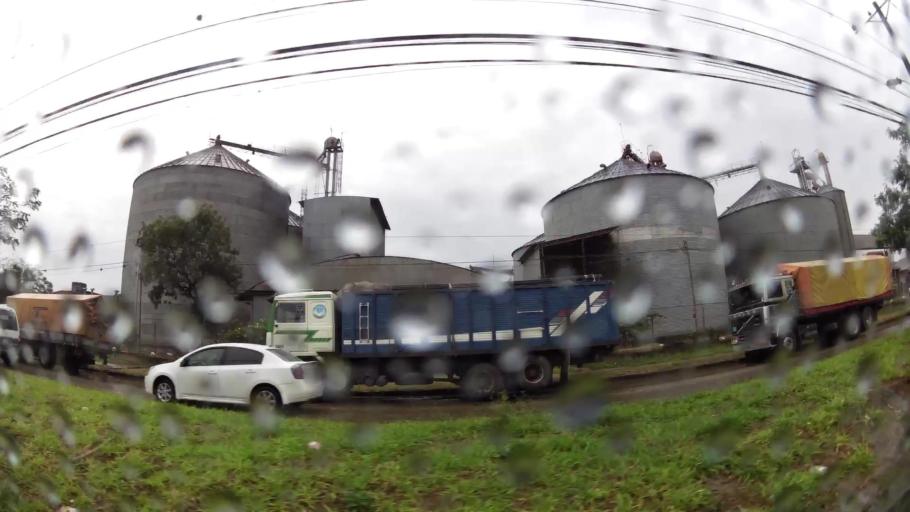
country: BO
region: Santa Cruz
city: Santa Cruz de la Sierra
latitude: -17.7564
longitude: -63.1372
